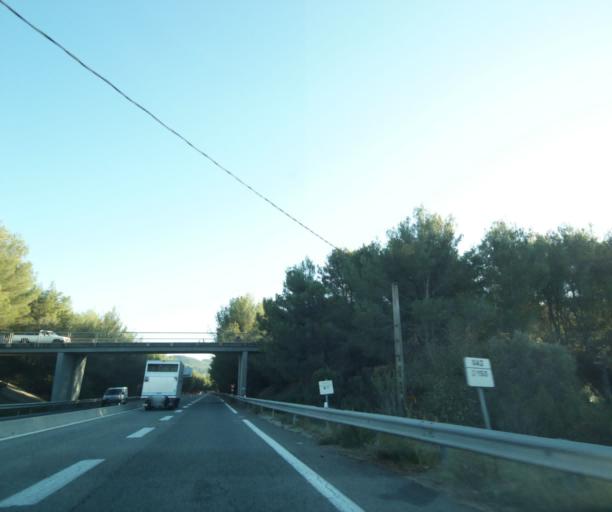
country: FR
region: Provence-Alpes-Cote d'Azur
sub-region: Departement du Var
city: Saint-Cyr-sur-Mer
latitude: 43.1924
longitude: 5.6904
